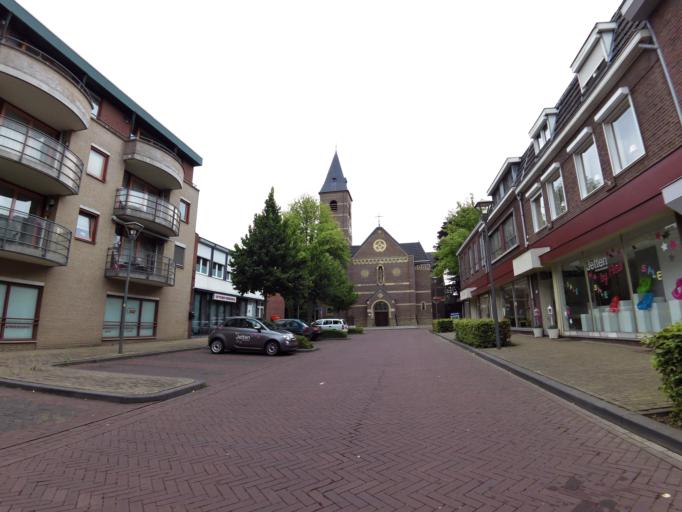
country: NL
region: Limburg
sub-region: Gemeente Kerkrade
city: Kerkrade
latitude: 50.8678
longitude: 6.0255
